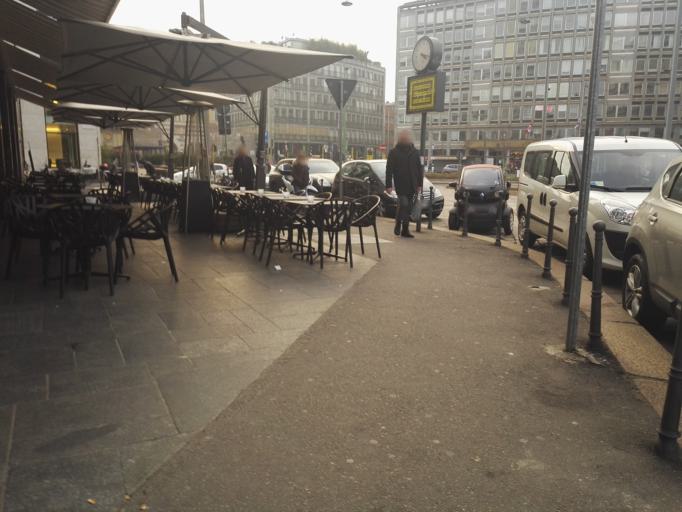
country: IT
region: Lombardy
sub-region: Citta metropolitana di Milano
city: Milano
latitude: 45.4728
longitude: 9.1962
